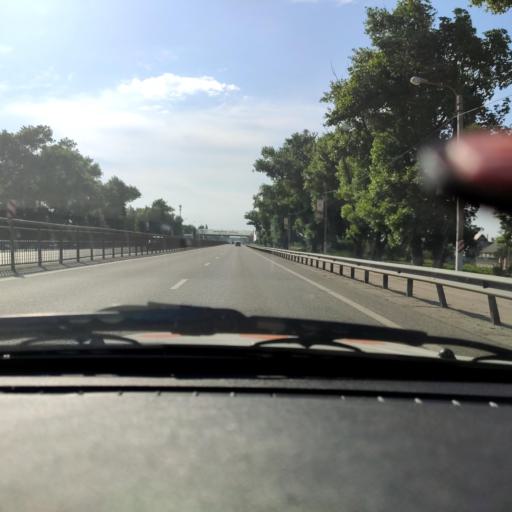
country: RU
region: Voronezj
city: Novaya Usman'
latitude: 51.6096
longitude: 39.3928
